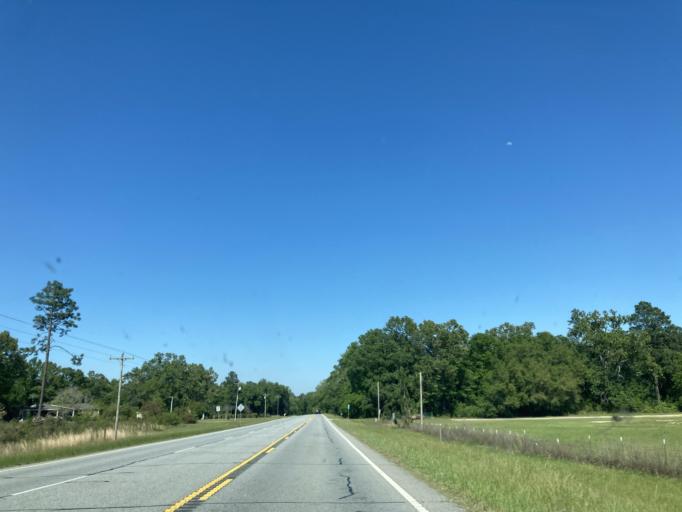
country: US
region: Georgia
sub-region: Baker County
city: Newton
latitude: 31.2913
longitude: -84.3543
